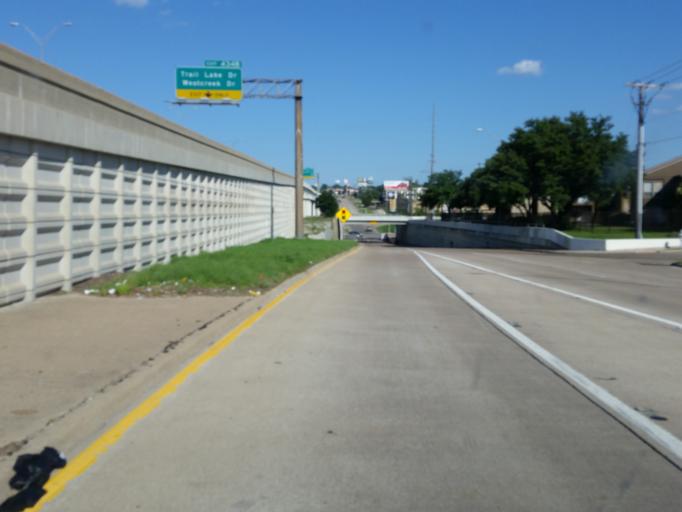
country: US
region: Texas
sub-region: Tarrant County
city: Edgecliff Village
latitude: 32.6760
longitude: -97.3834
